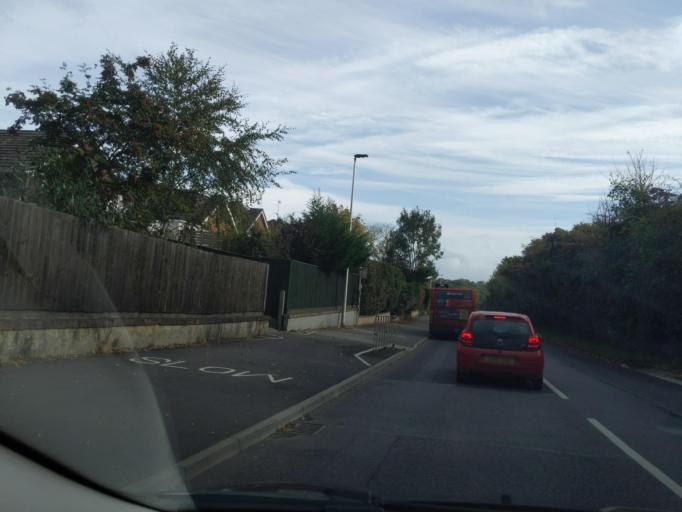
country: GB
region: England
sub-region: Devon
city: Newton Abbot
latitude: 50.5341
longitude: -3.6325
